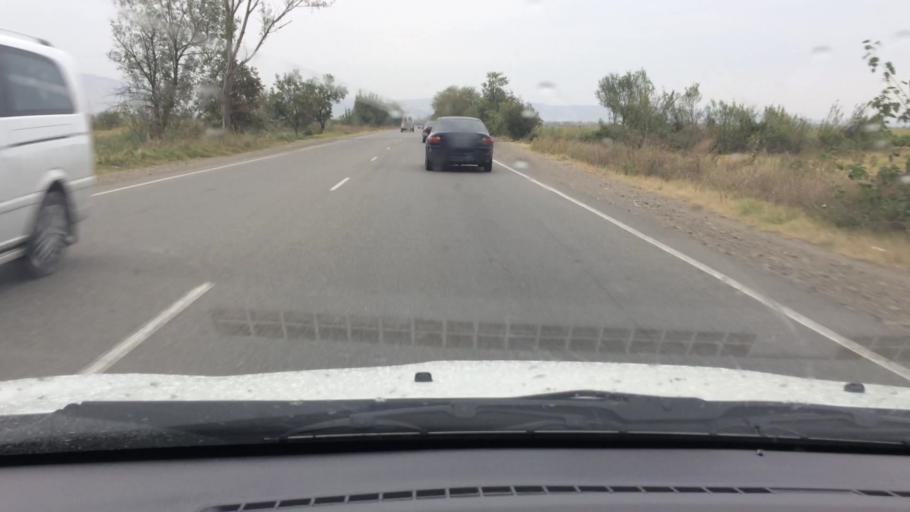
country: GE
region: Kvemo Kartli
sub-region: Marneuli
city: Marneuli
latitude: 41.5575
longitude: 44.7760
